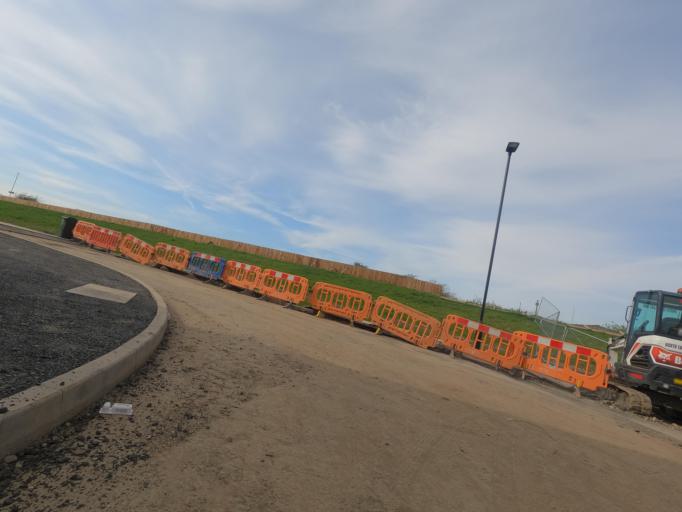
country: GB
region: England
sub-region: Newcastle upon Tyne
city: Hazlerigg
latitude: 55.0449
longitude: -1.6458
